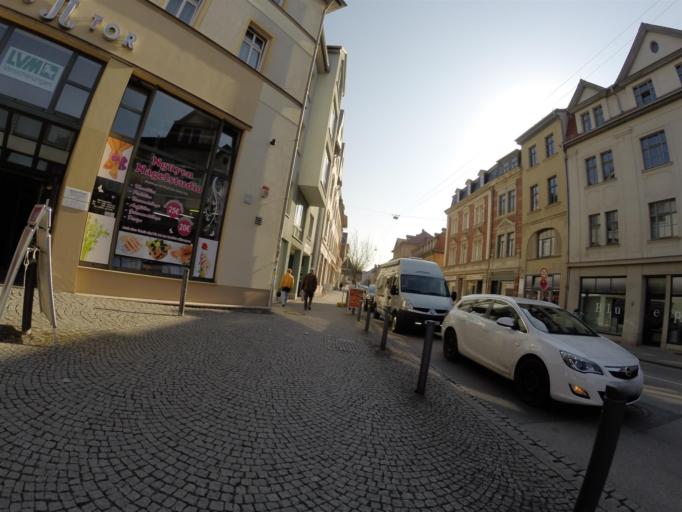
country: DE
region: Thuringia
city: Weimar
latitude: 50.9841
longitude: 11.3260
